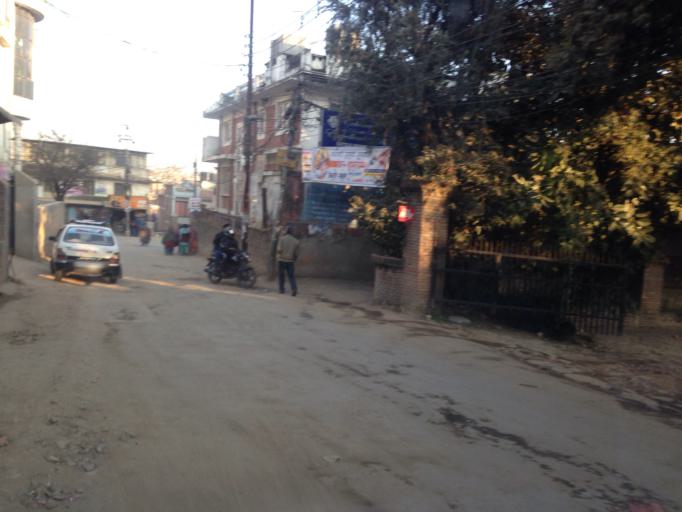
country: NP
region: Central Region
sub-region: Bagmati Zone
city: Kathmandu
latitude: 27.7128
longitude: 85.3002
